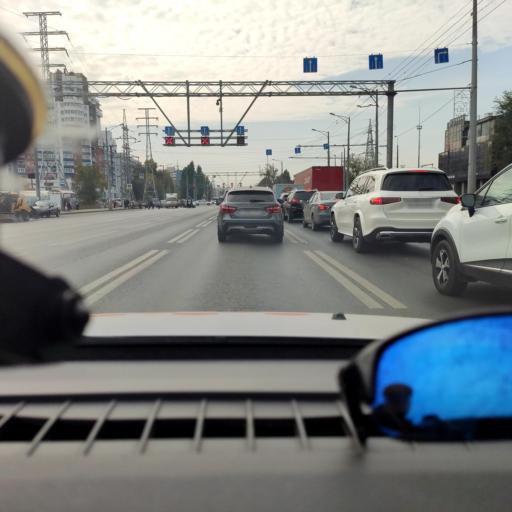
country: RU
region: Samara
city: Samara
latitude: 53.2426
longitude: 50.2104
